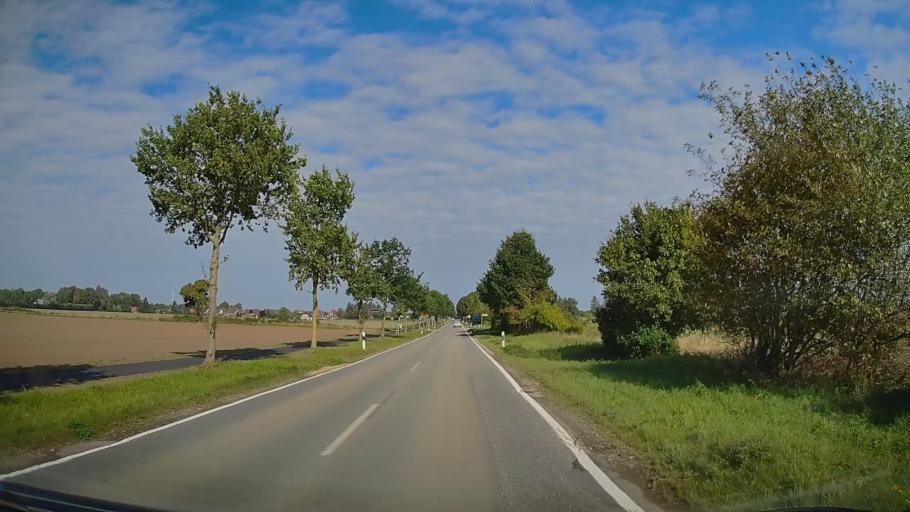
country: DE
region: Schleswig-Holstein
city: Oldenburg in Holstein
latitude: 54.3120
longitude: 10.8869
